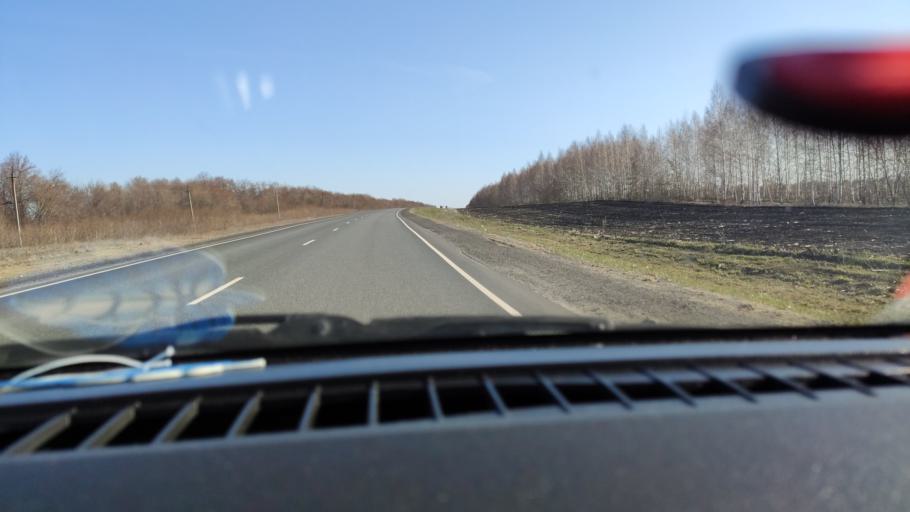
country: RU
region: Samara
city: Varlamovo
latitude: 52.9784
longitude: 48.3109
